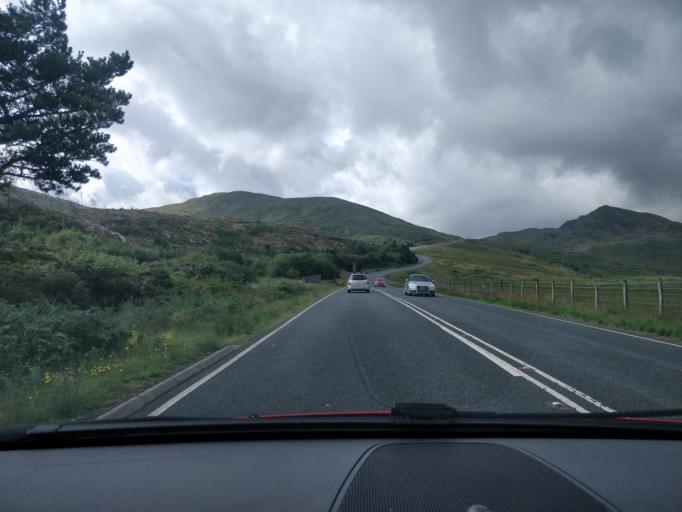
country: GB
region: Wales
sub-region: Gwynedd
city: Blaenau-Ffestiniog
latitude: 53.0377
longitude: -3.9259
